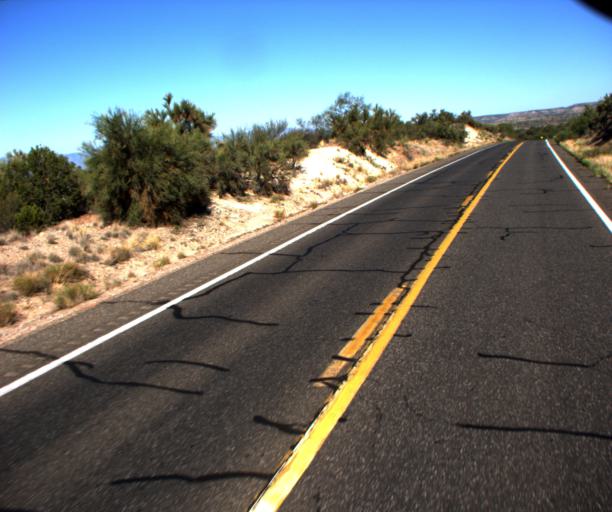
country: US
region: Arizona
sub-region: Yavapai County
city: Lake Montezuma
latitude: 34.6987
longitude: -111.7619
